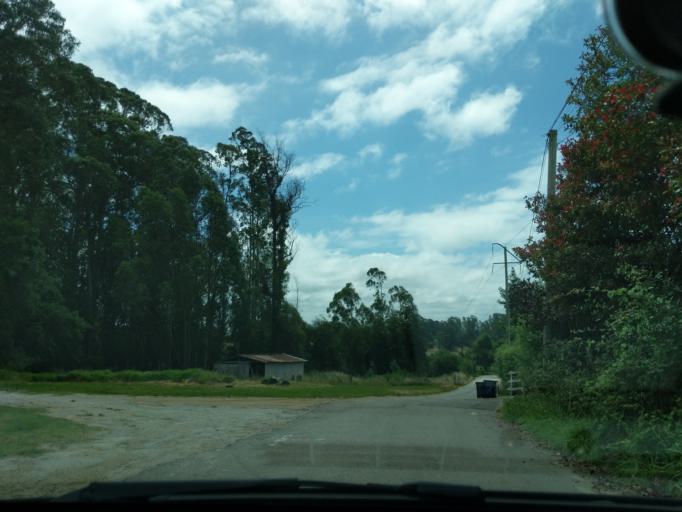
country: US
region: California
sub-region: Santa Cruz County
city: Aptos Hills-Larkin Valley
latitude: 36.9449
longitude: -121.8106
